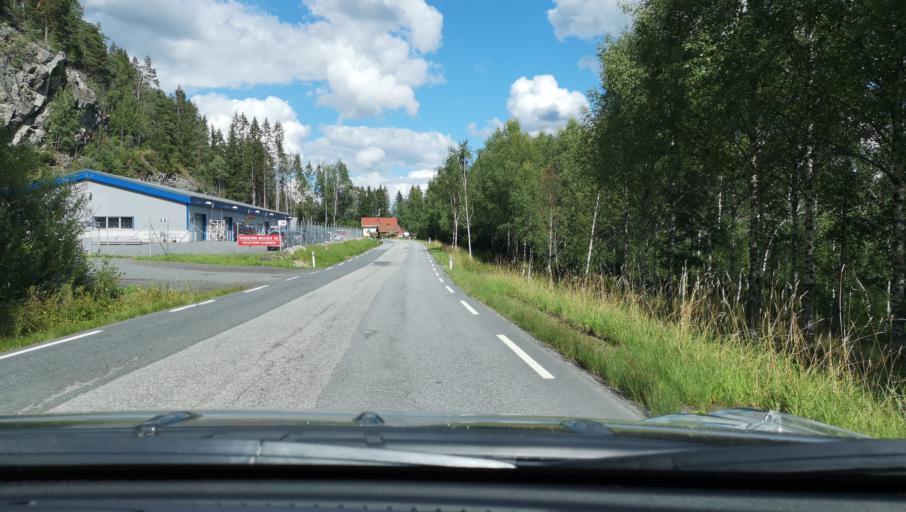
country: NO
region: Ostfold
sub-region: Hobol
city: Elvestad
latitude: 59.6373
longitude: 10.9642
